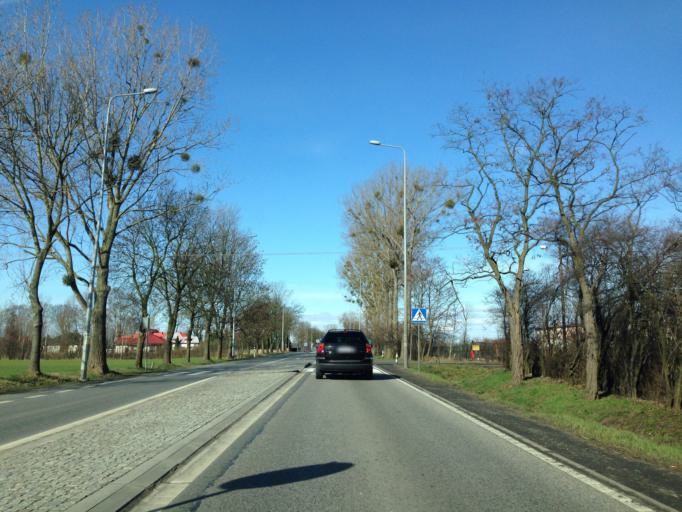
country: PL
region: Pomeranian Voivodeship
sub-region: Powiat malborski
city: Malbork
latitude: 54.0429
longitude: 18.9883
